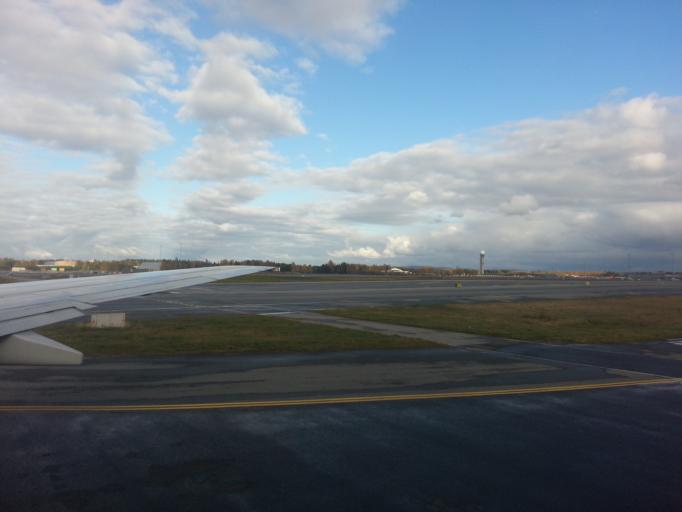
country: NO
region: Akershus
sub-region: Nannestad
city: Teigebyen
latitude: 60.1979
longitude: 11.0872
